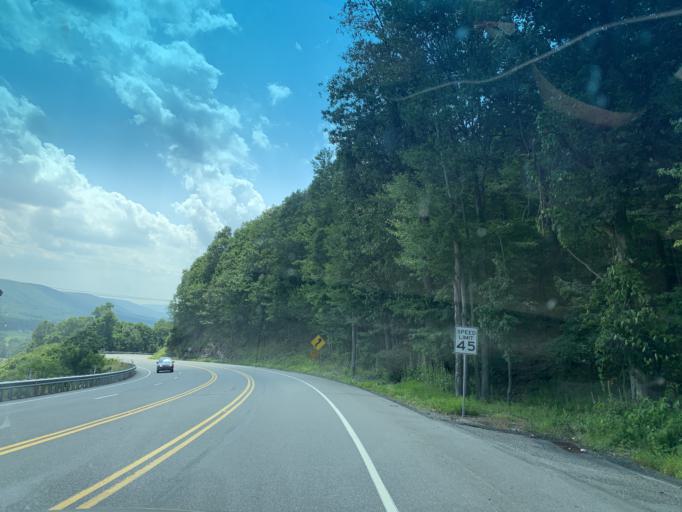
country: US
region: Pennsylvania
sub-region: Schuylkill County
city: Girardville
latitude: 40.7776
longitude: -76.2713
